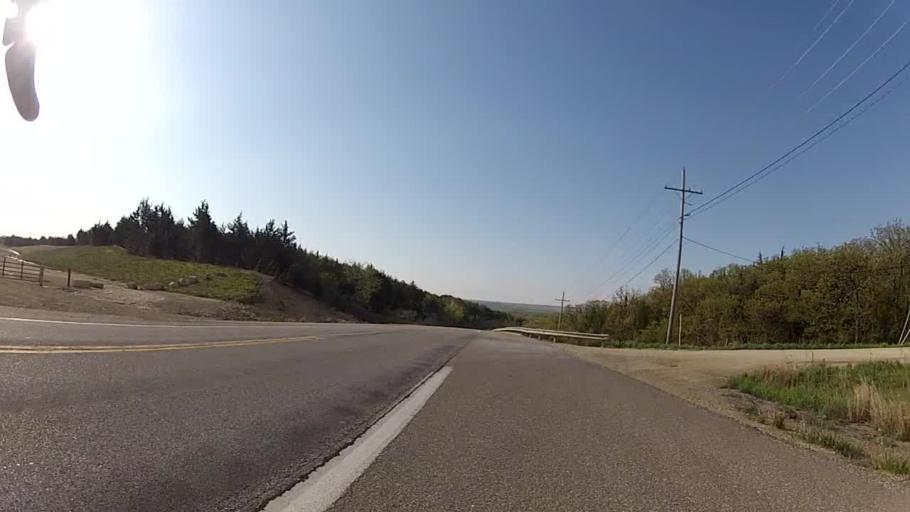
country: US
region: Kansas
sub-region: Riley County
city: Manhattan
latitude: 39.1745
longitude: -96.6467
